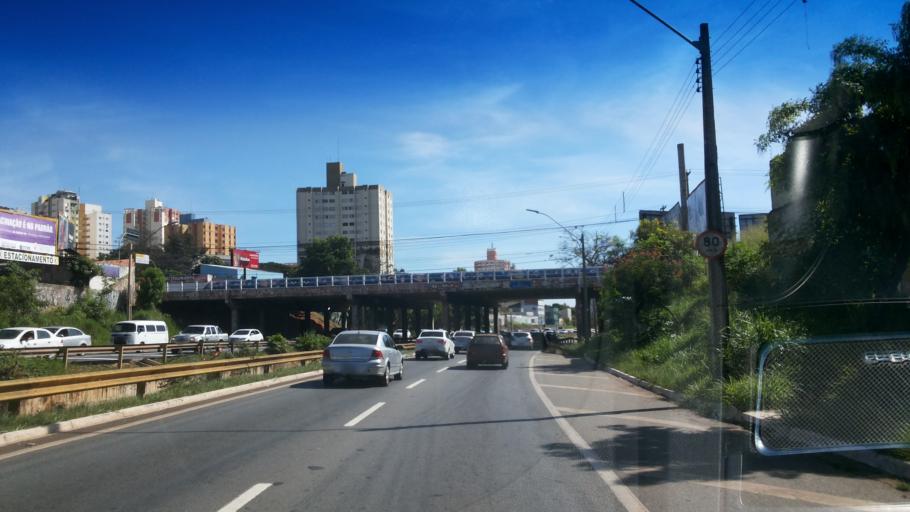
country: BR
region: Goias
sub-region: Goiania
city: Goiania
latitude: -16.6793
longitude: -49.2490
